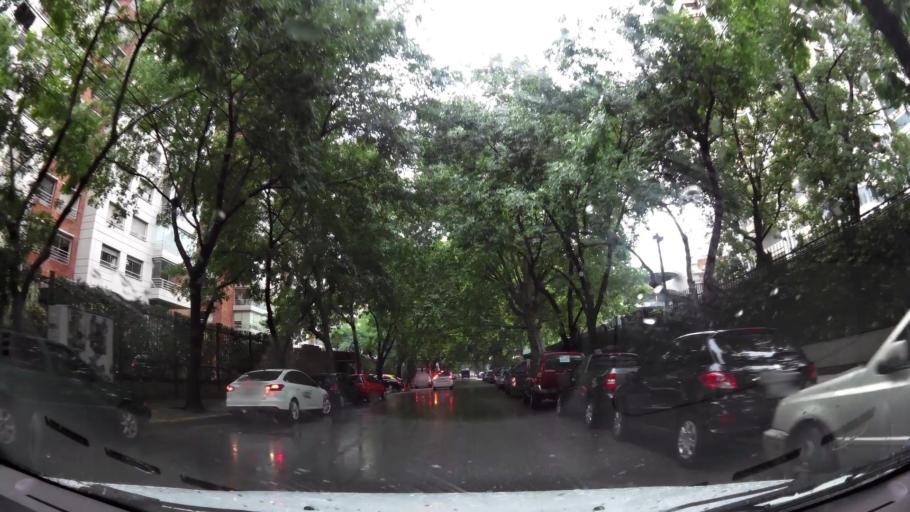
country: AR
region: Buenos Aires F.D.
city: Colegiales
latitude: -34.5753
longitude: -58.4222
